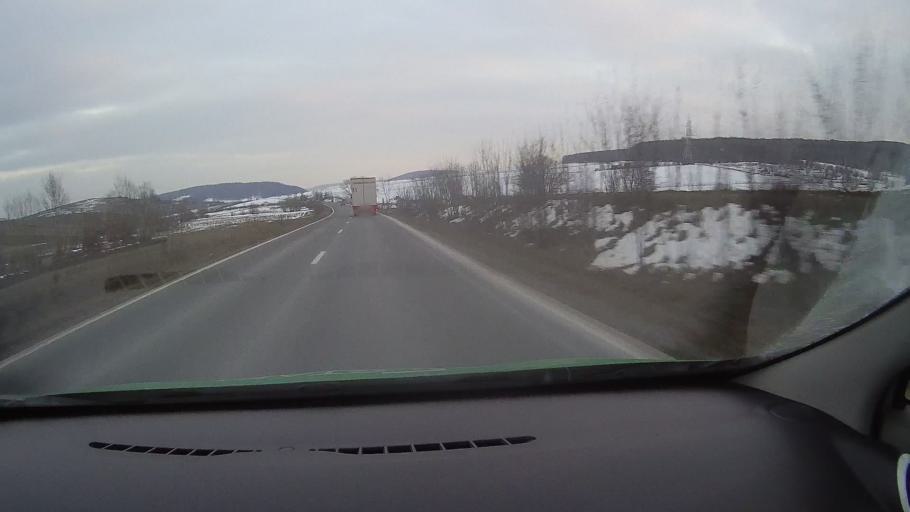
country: RO
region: Harghita
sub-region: Comuna Lupeni
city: Lupeni
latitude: 46.3543
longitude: 25.2537
